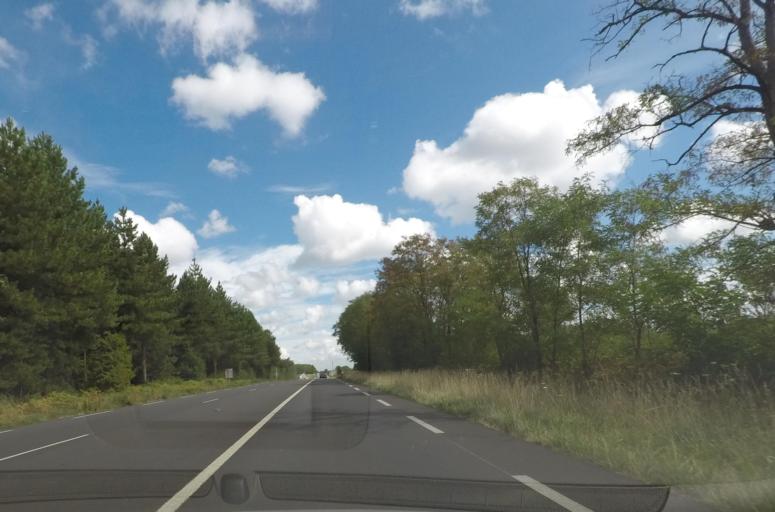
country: FR
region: Pays de la Loire
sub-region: Departement de la Sarthe
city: Clermont-Creans
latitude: 47.7601
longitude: 0.0138
